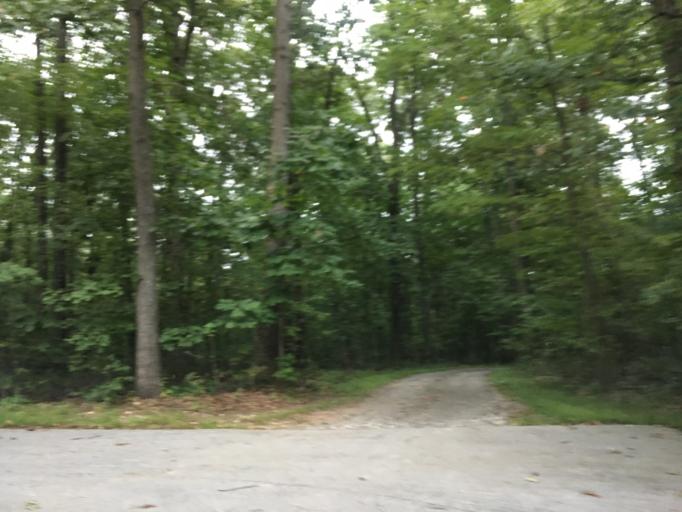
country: US
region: Maryland
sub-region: Baltimore County
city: Hunt Valley
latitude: 39.5809
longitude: -76.6819
